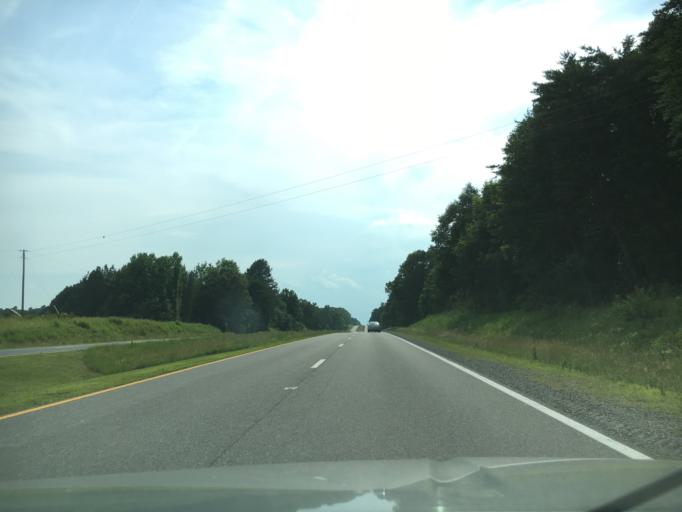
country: US
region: Virginia
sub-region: Halifax County
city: Halifax
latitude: 36.8241
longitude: -78.7054
